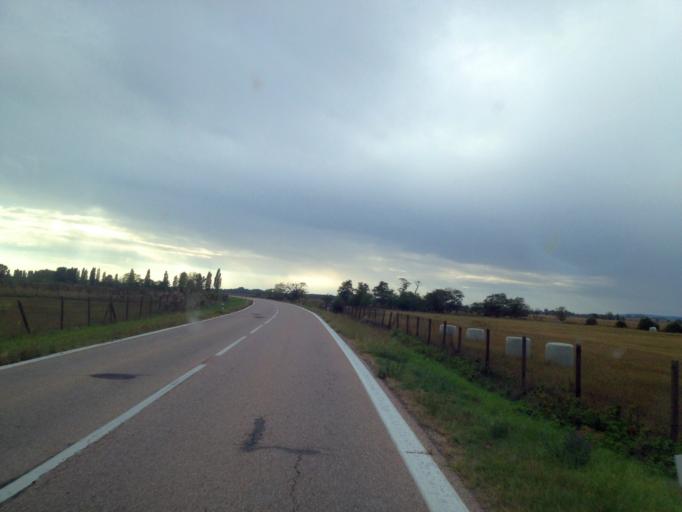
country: HU
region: Komarom-Esztergom
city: Sutto
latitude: 47.7787
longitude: 18.4517
